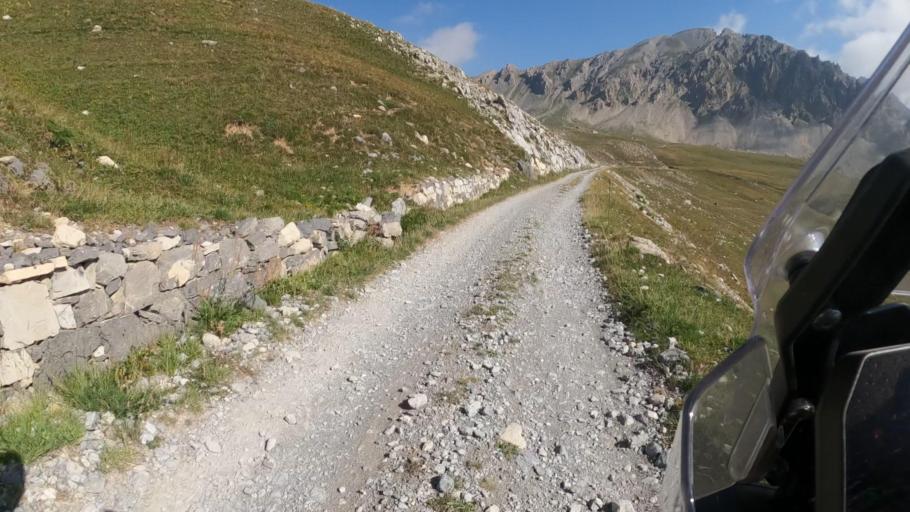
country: IT
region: Piedmont
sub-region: Provincia di Cuneo
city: Bersezio
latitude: 44.4016
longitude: 7.0159
